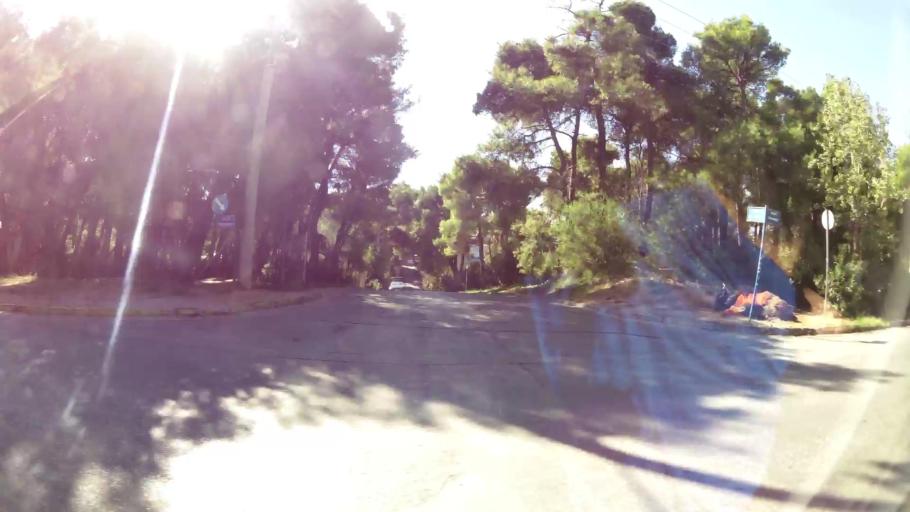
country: GR
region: Attica
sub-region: Nomarchia Athinas
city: Ekali
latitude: 38.1179
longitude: 23.8349
